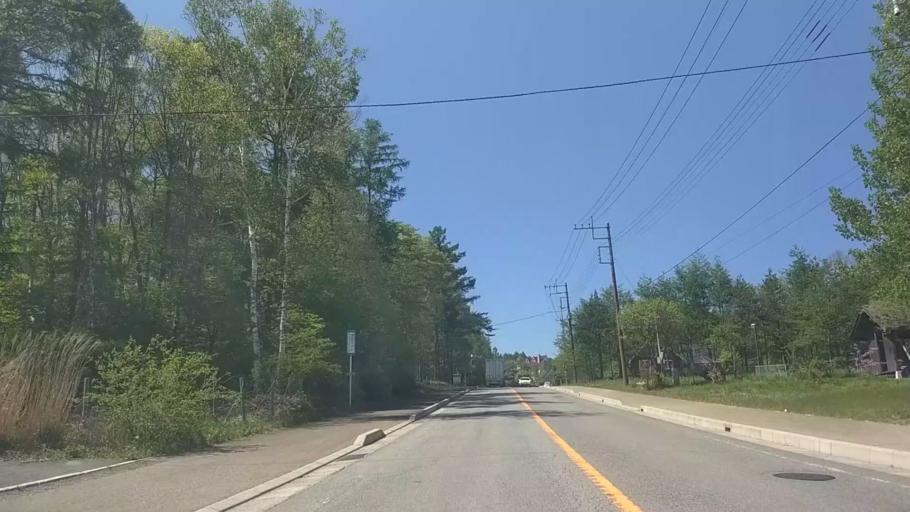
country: JP
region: Yamanashi
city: Nirasaki
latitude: 35.9174
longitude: 138.4410
